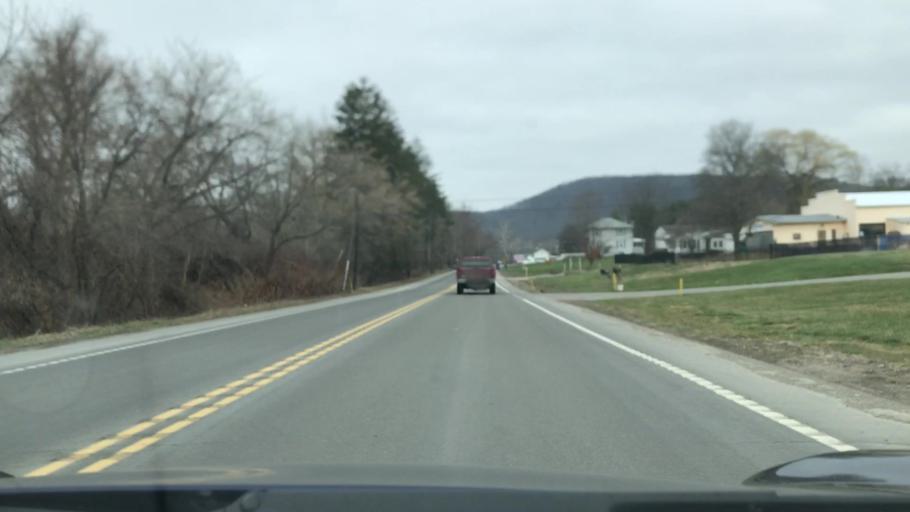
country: US
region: Pennsylvania
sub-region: Bradford County
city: Towanda
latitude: 41.7753
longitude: -76.3761
